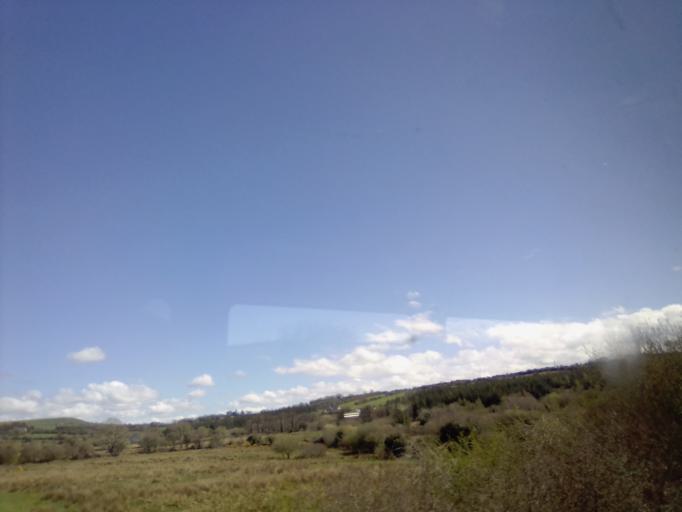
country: IE
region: Munster
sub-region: Ciarrai
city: Cill Airne
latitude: 52.1574
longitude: -9.5831
